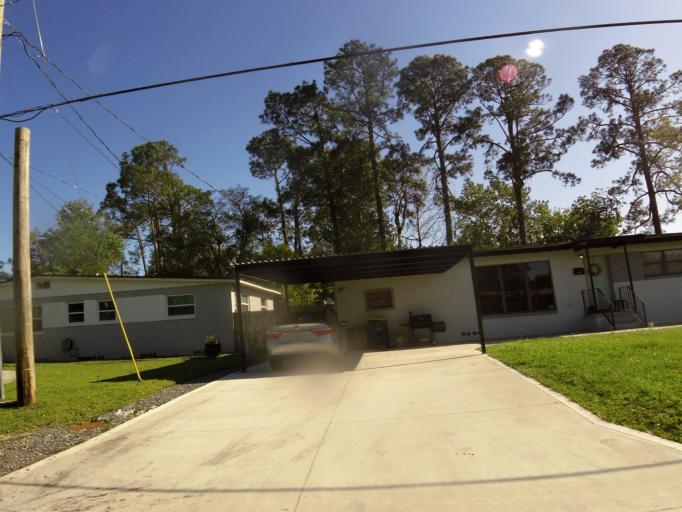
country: US
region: Florida
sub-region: Duval County
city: Jacksonville
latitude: 30.2812
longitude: -81.5940
